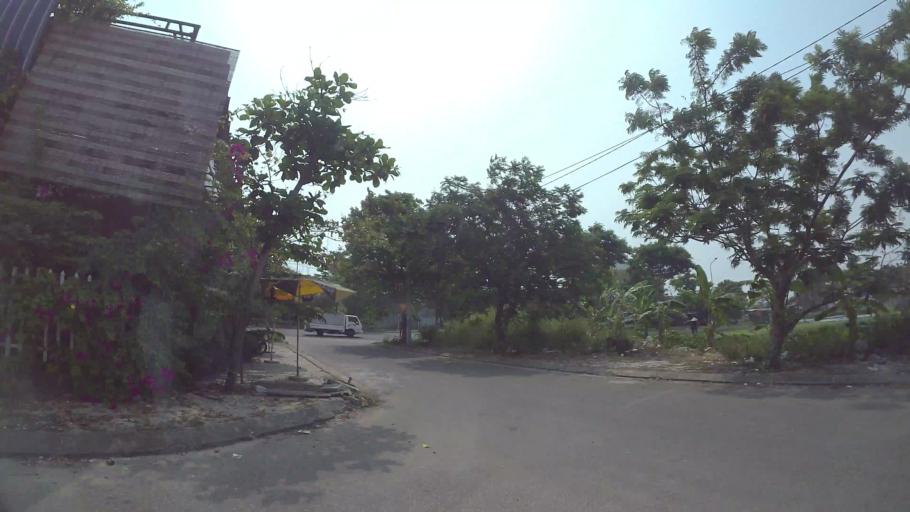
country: VN
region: Da Nang
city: Da Nang
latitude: 16.0930
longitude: 108.2380
